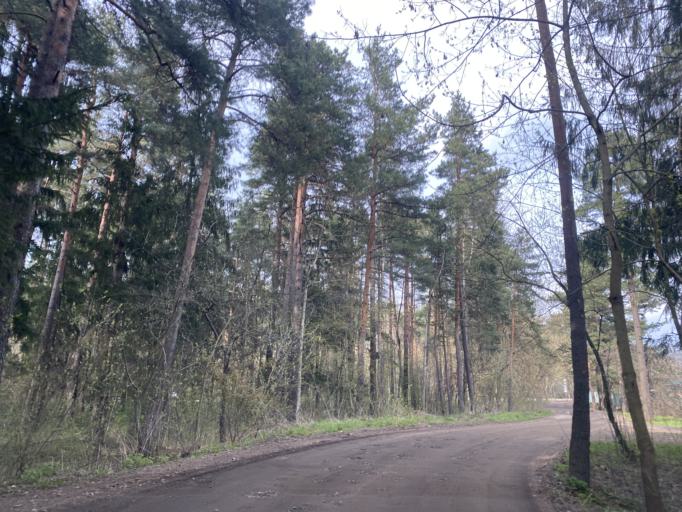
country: BY
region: Minsk
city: Vyaliki Trastsyanets
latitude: 53.9160
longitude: 27.6628
